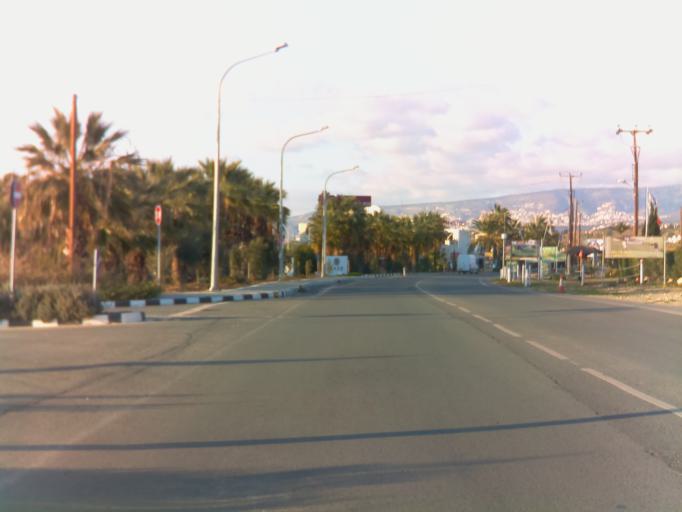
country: CY
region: Pafos
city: Kissonerga
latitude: 34.8085
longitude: 32.3965
